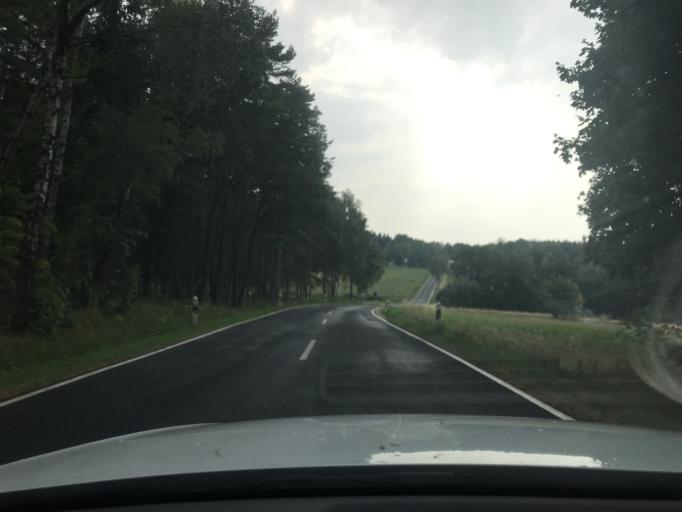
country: DE
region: Bavaria
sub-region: Upper Franconia
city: Prebitz
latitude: 49.7983
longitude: 11.6576
